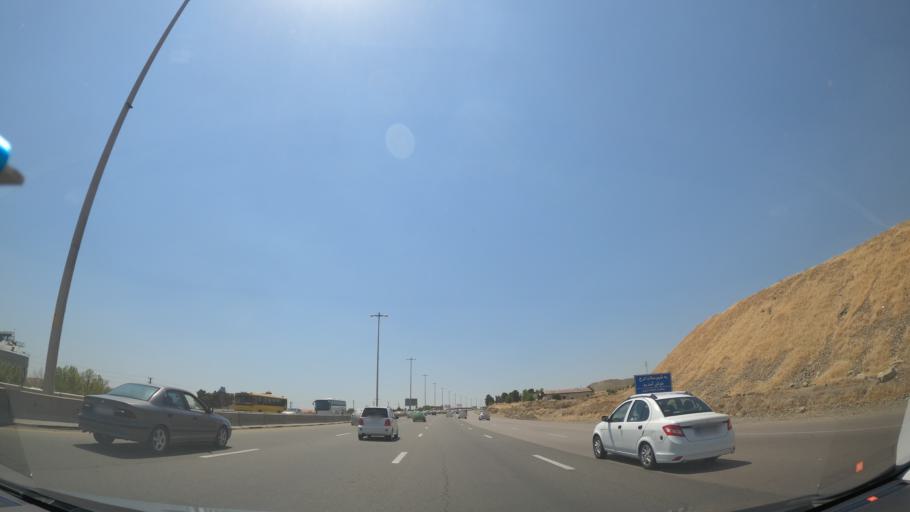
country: IR
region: Tehran
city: Shahr-e Qods
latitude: 35.7441
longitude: 51.0979
